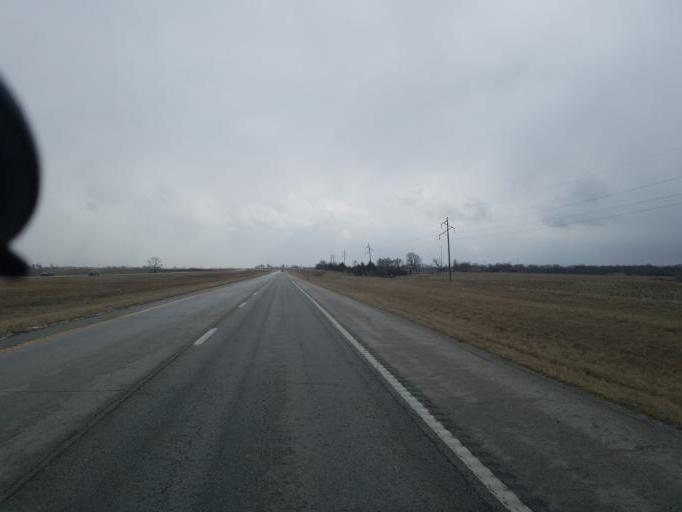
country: US
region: Missouri
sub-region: Randolph County
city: Moberly
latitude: 39.5389
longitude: -92.4490
